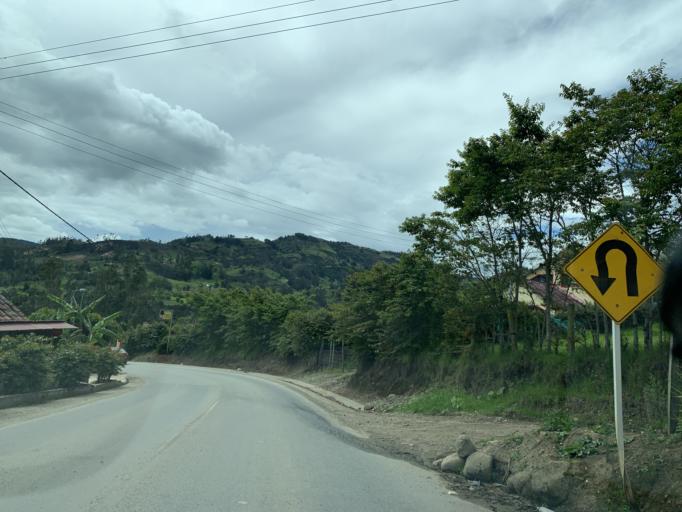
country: CO
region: Boyaca
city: Ramiriqui
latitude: 5.4104
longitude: -73.3314
